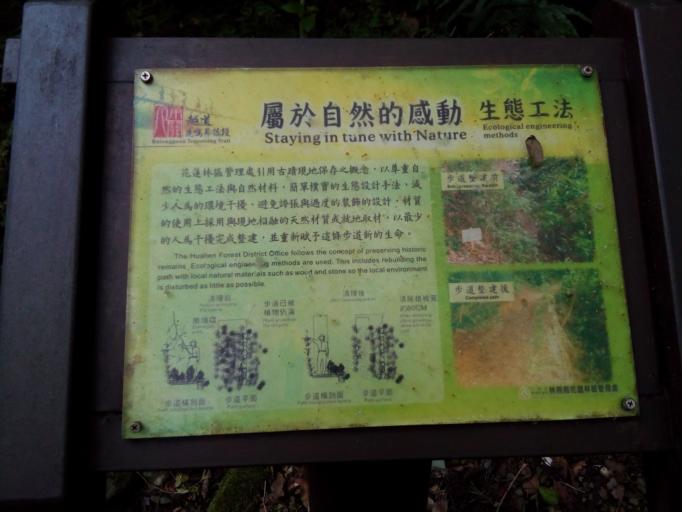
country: TW
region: Taiwan
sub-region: Taitung
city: Taitung
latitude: 23.3180
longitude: 121.2563
